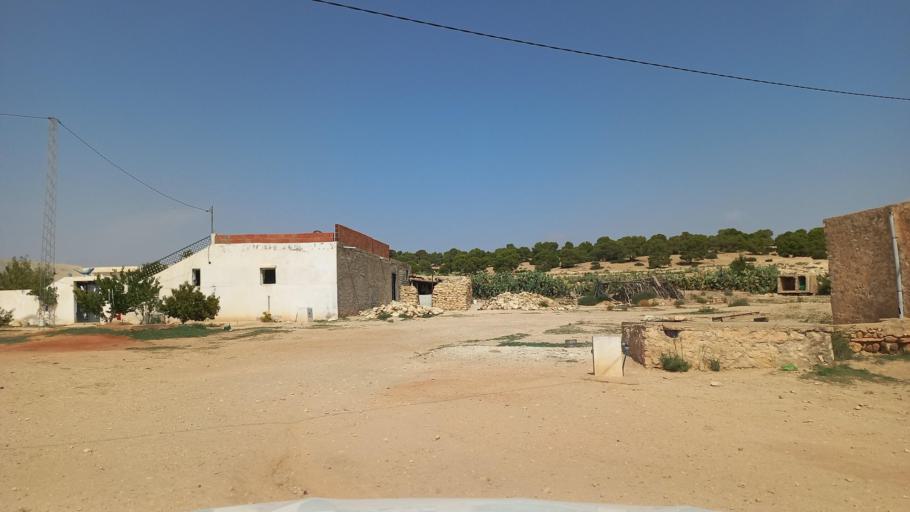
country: TN
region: Al Qasrayn
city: Sbiba
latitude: 35.3992
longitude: 8.9578
